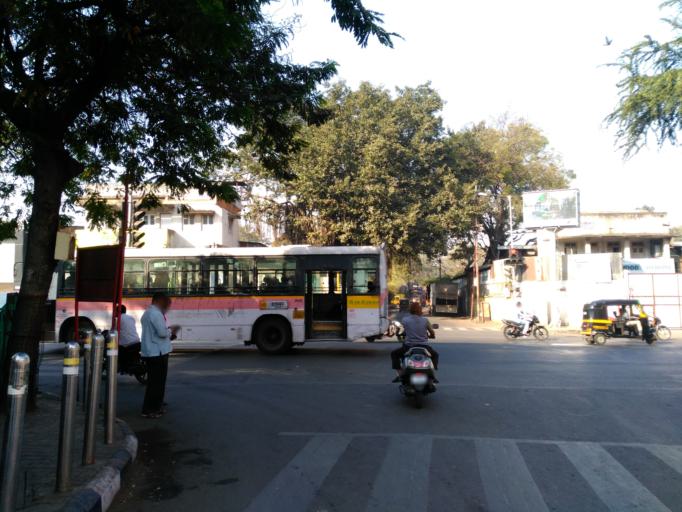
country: IN
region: Maharashtra
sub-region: Pune Division
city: Pune
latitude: 18.5072
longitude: 73.8686
